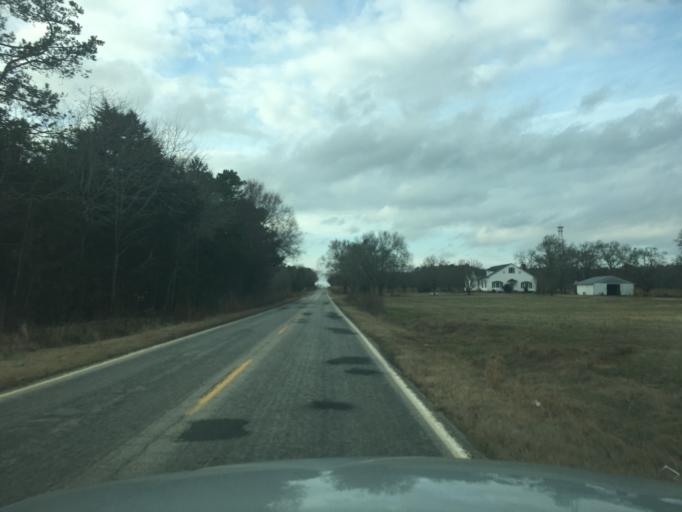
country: US
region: South Carolina
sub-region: Abbeville County
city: Due West
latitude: 34.3231
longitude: -82.4701
